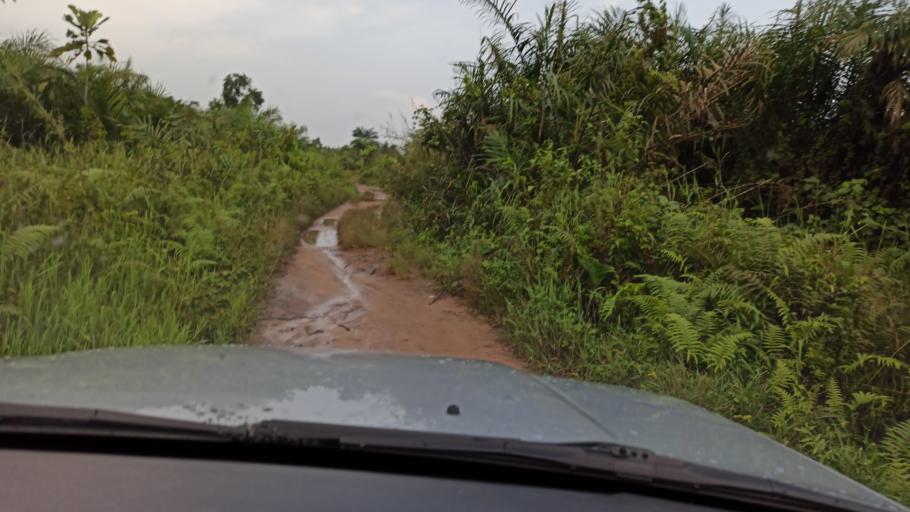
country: BJ
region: Queme
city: Porto-Novo
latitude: 6.4550
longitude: 2.6723
